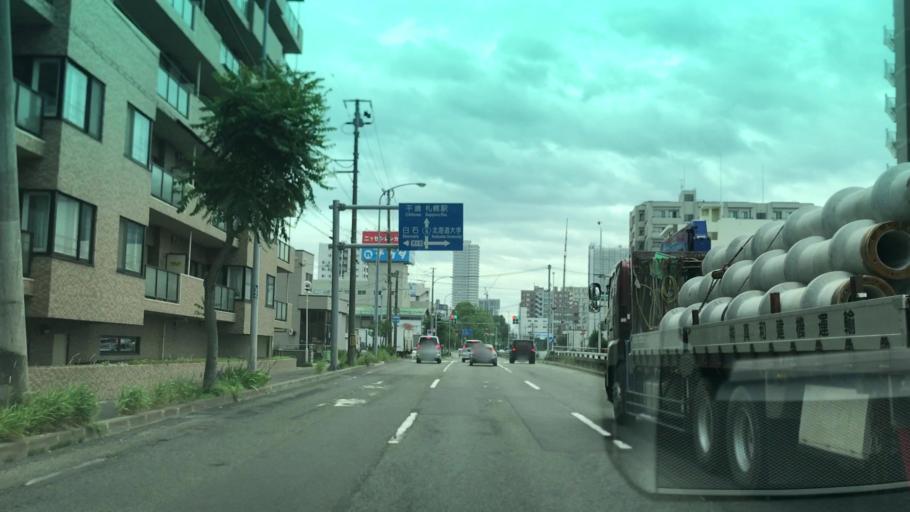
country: JP
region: Hokkaido
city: Sapporo
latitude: 43.0797
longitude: 141.3518
